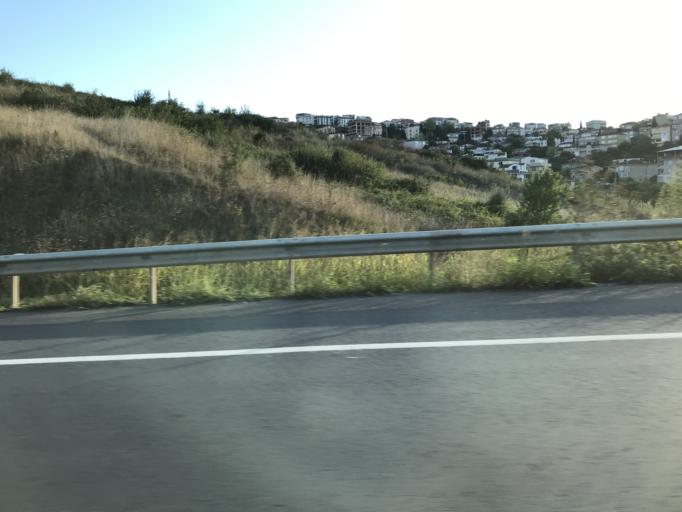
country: TR
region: Kocaeli
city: Darica
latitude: 40.7781
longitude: 29.4189
